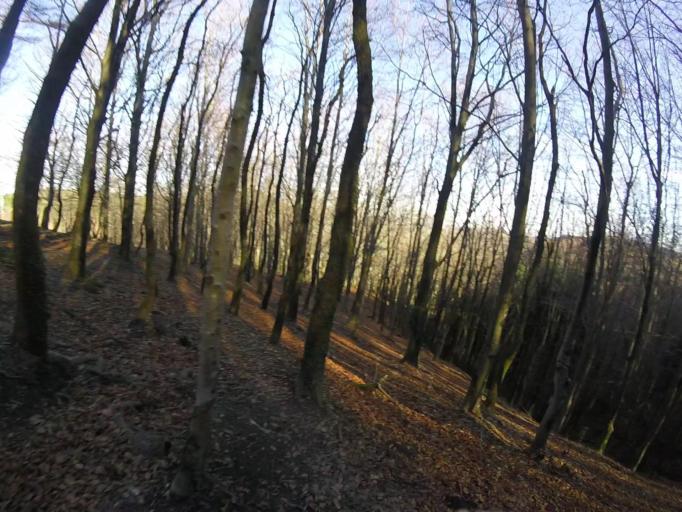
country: ES
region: Basque Country
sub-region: Provincia de Guipuzcoa
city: Irun
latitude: 43.2934
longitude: -1.7849
